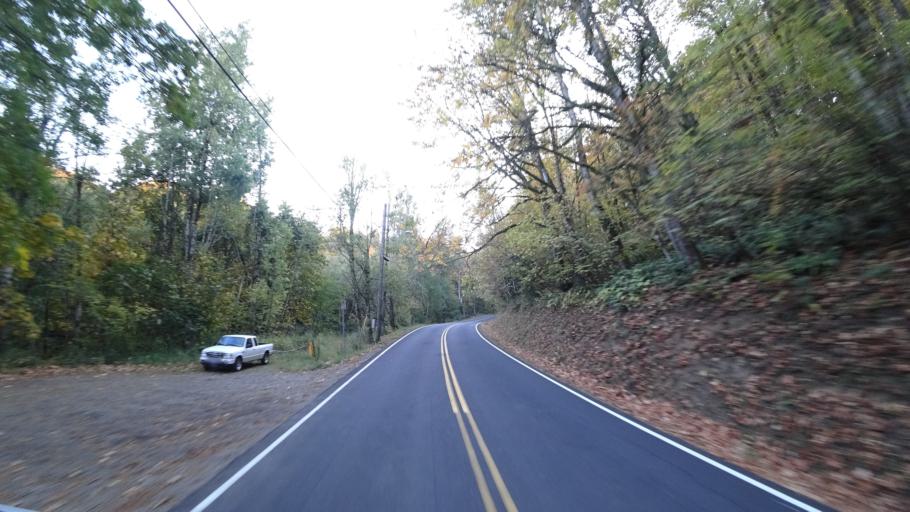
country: US
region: Oregon
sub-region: Multnomah County
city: Gresham
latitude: 45.4879
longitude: -122.4337
